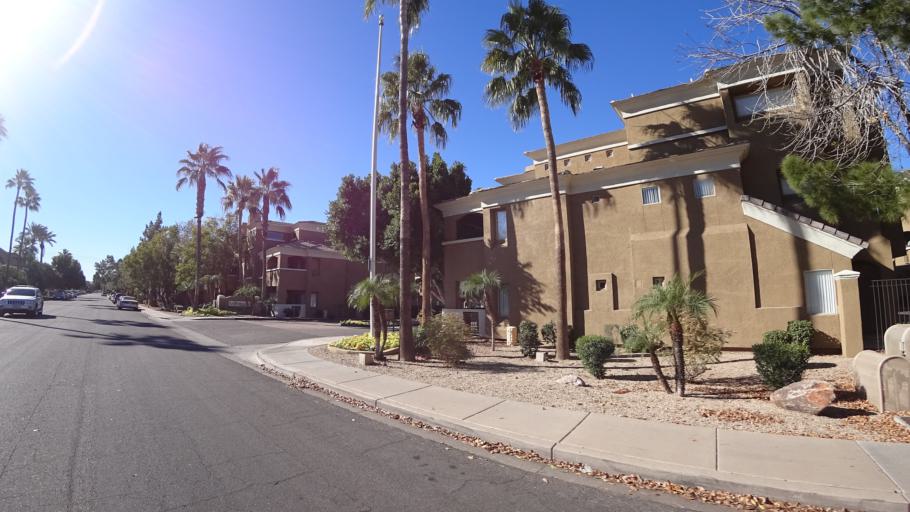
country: US
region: Arizona
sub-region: Maricopa County
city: Phoenix
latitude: 33.5034
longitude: -112.0346
